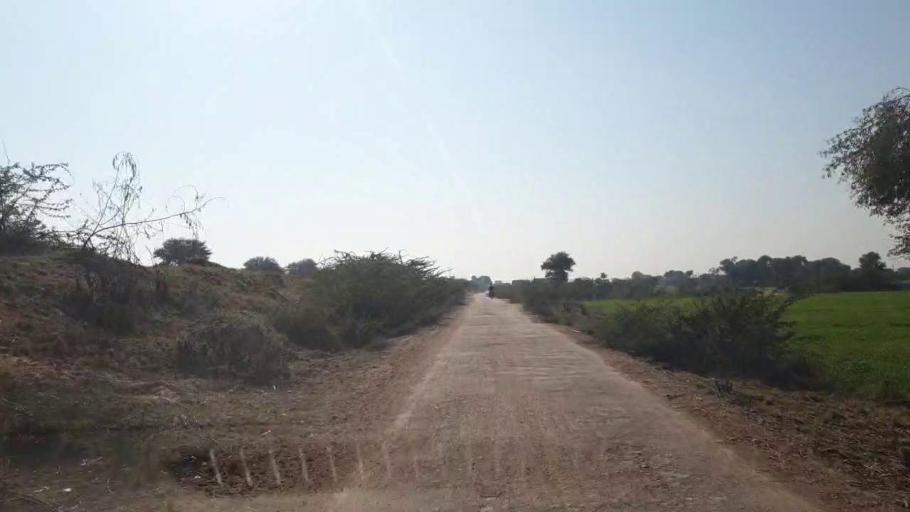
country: PK
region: Sindh
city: Shahpur Chakar
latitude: 26.0818
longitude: 68.6476
